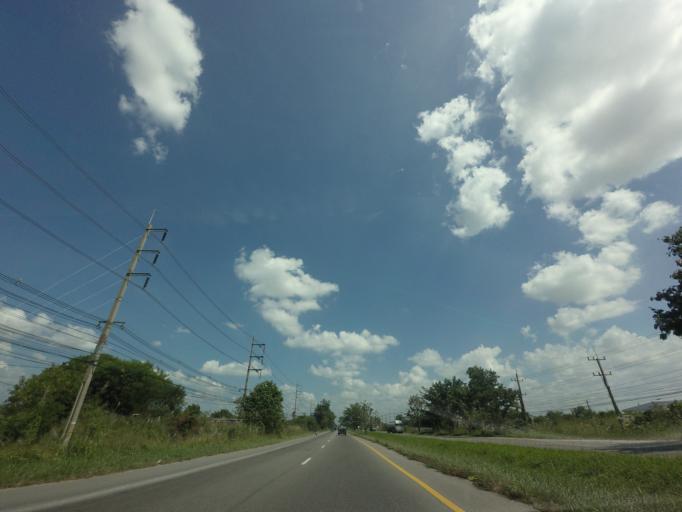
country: TH
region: Chon Buri
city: Ban Bueng
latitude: 13.2998
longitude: 101.1510
